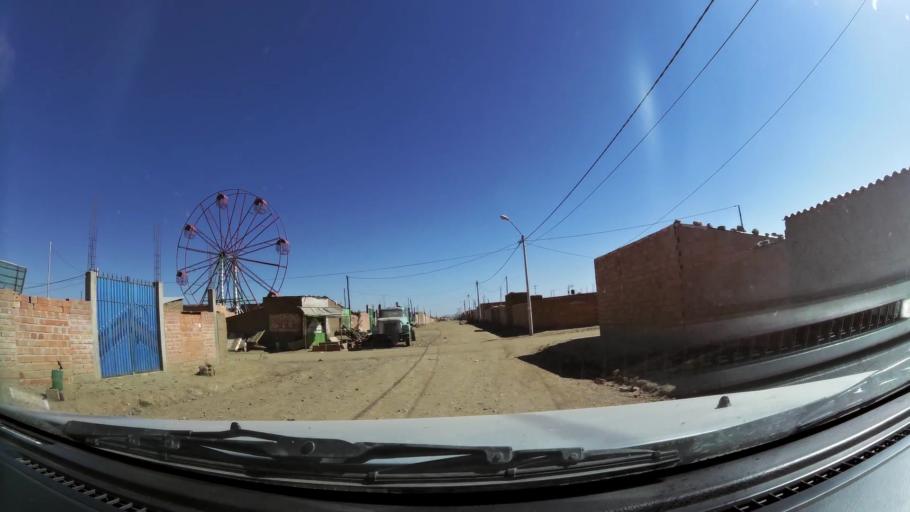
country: BO
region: La Paz
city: La Paz
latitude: -16.6119
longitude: -68.1969
